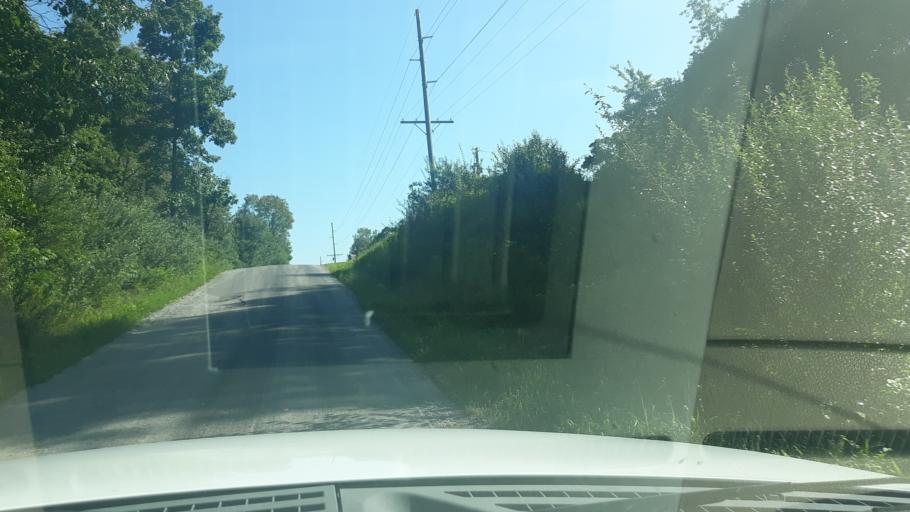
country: US
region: Illinois
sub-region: Saline County
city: Harrisburg
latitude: 37.8565
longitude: -88.5963
